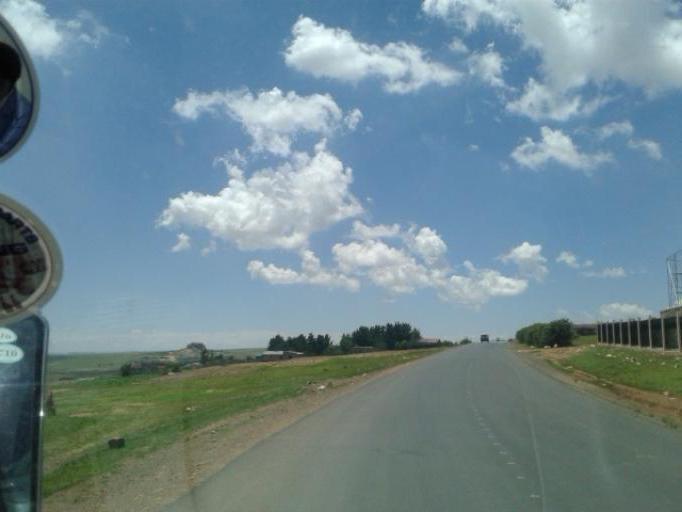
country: LS
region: Maseru
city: Maseru
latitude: -29.3184
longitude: 27.5850
